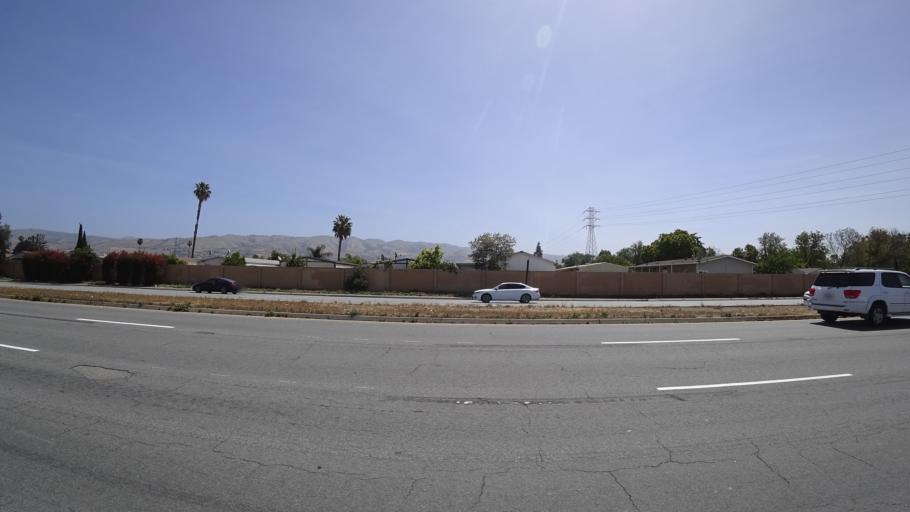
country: US
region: California
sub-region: Santa Clara County
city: Seven Trees
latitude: 37.3184
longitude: -121.8082
